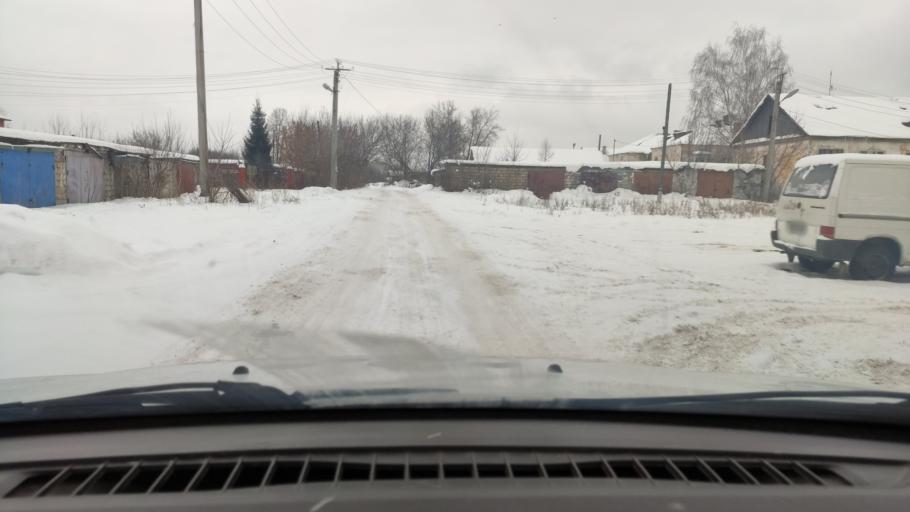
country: RU
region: Perm
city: Kungur
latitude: 57.4489
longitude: 56.9296
